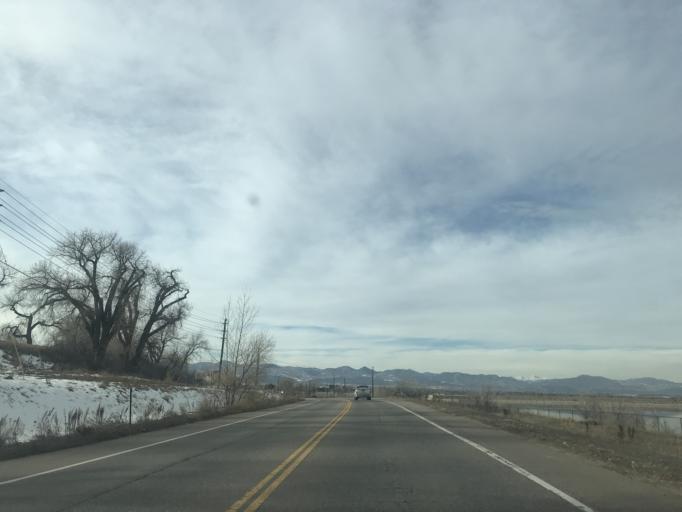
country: US
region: Colorado
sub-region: Arapahoe County
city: Columbine Valley
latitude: 39.5659
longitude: -105.0147
